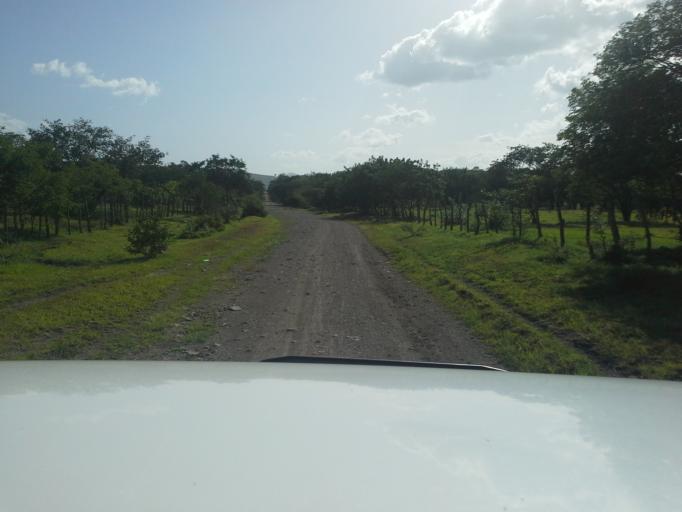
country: NI
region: Matagalpa
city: Ciudad Dario
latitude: 12.6612
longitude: -86.0684
